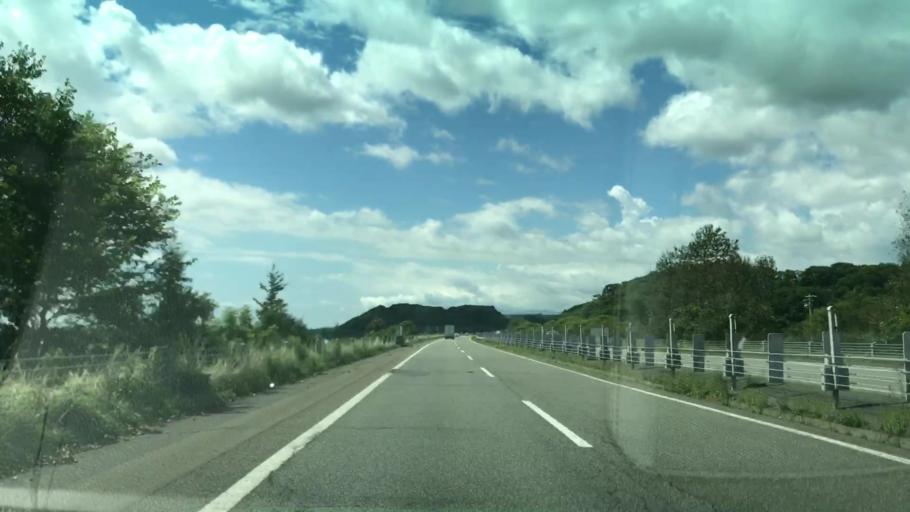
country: JP
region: Hokkaido
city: Shiraoi
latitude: 42.5843
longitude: 141.4113
